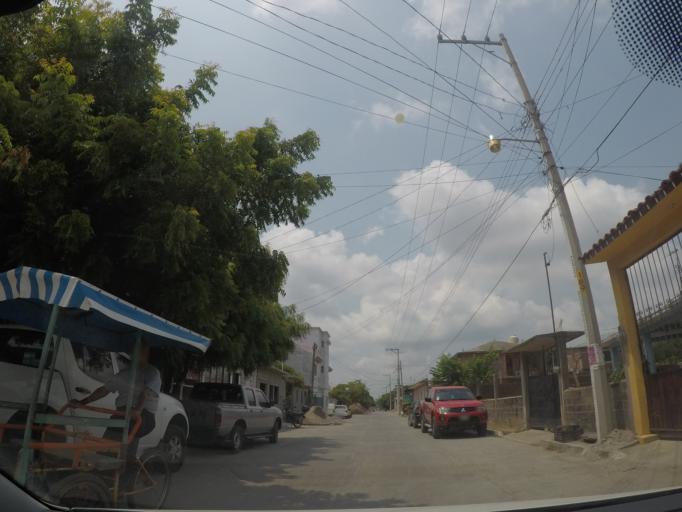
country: MX
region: Oaxaca
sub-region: El Espinal
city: El Espinal
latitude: 16.4800
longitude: -95.0430
